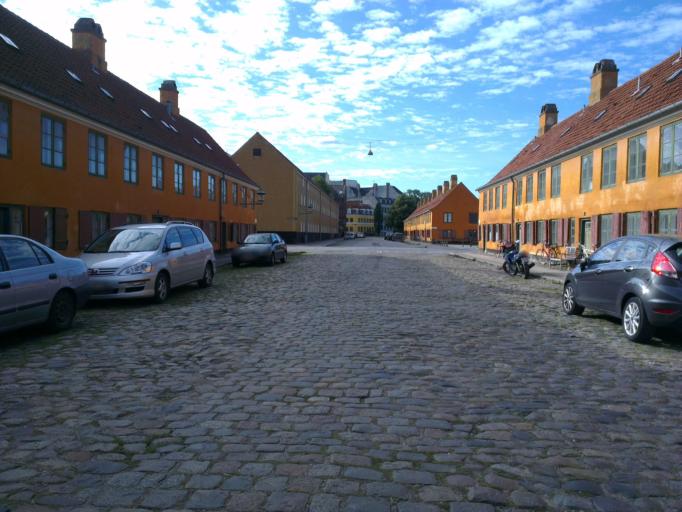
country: DK
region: Capital Region
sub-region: Kobenhavn
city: Christianshavn
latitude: 55.6890
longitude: 12.5869
